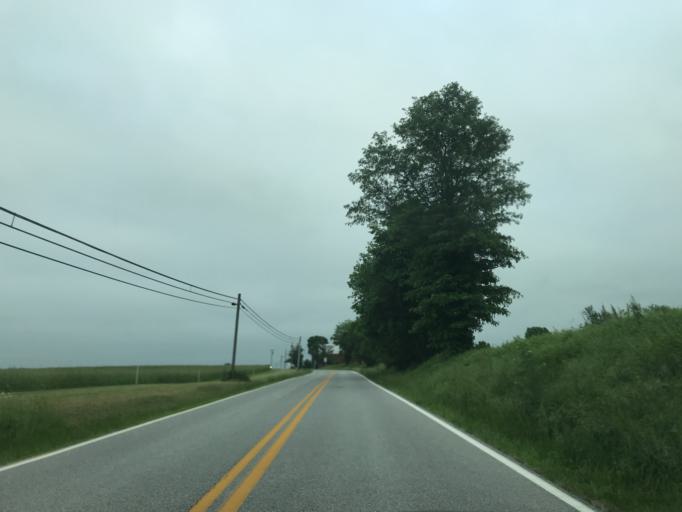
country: US
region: Maryland
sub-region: Frederick County
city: Emmitsburg
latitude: 39.6848
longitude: -77.3243
